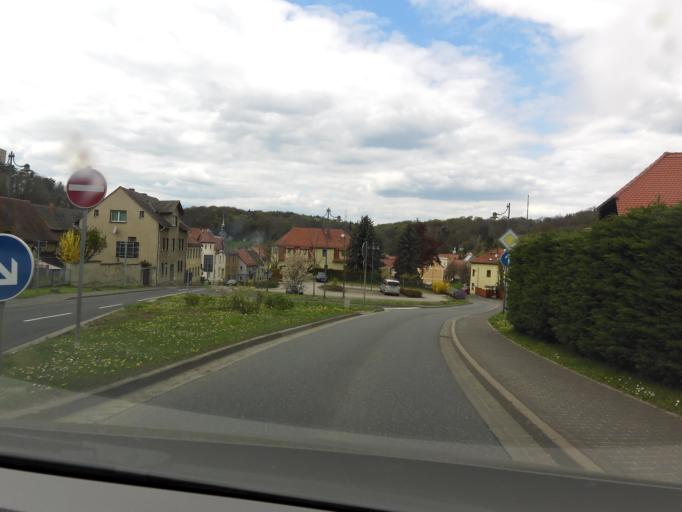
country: DE
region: Saxony-Anhalt
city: Eckartsberga
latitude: 51.1218
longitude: 11.5640
